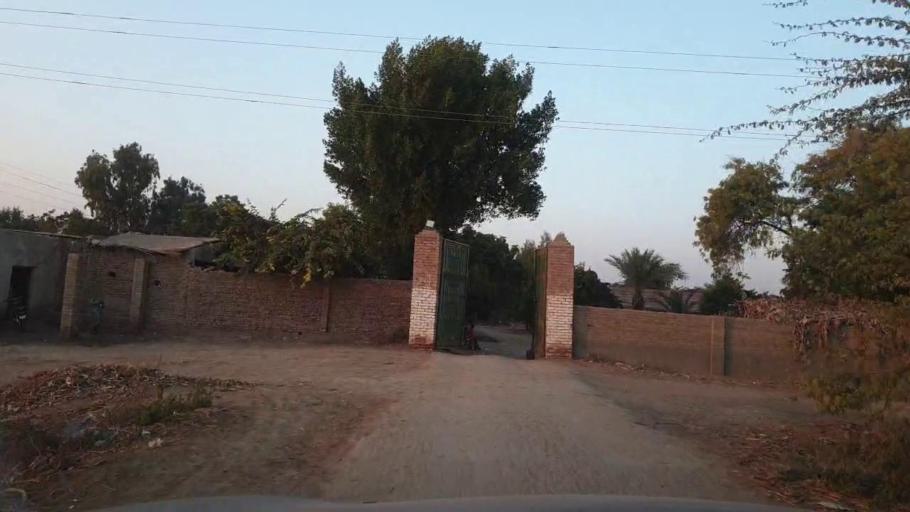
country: PK
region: Sindh
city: Mirpur Khas
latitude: 25.5989
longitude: 68.8523
